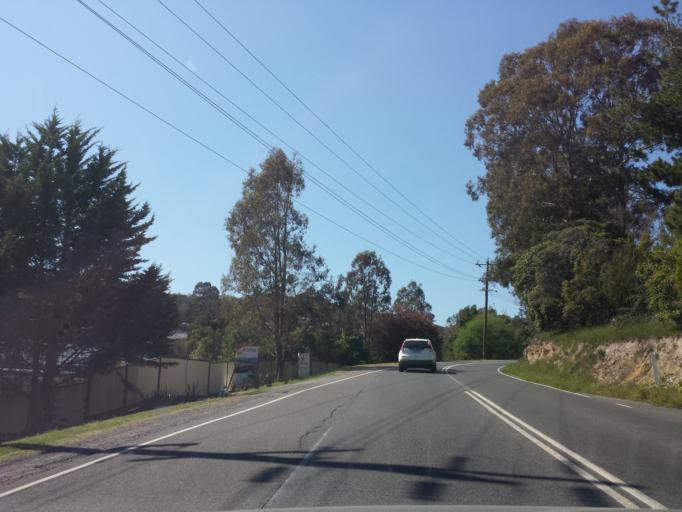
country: AU
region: Victoria
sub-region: Yarra Ranges
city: Lilydale
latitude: -37.7643
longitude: 145.3621
